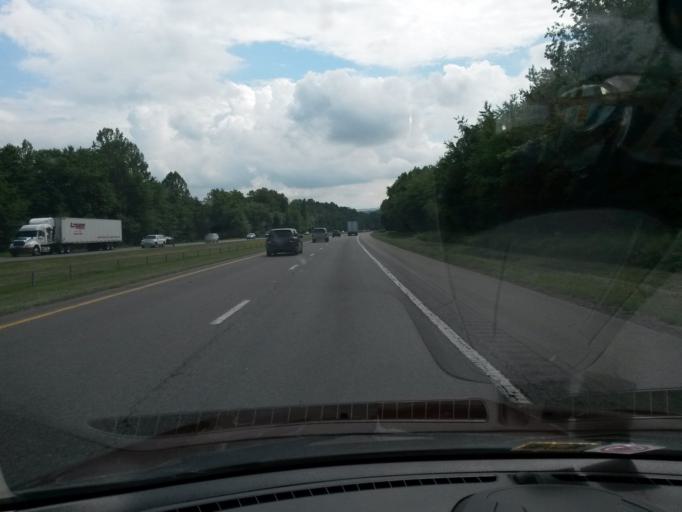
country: US
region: North Carolina
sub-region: Surry County
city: Elkin
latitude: 36.3222
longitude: -80.7968
